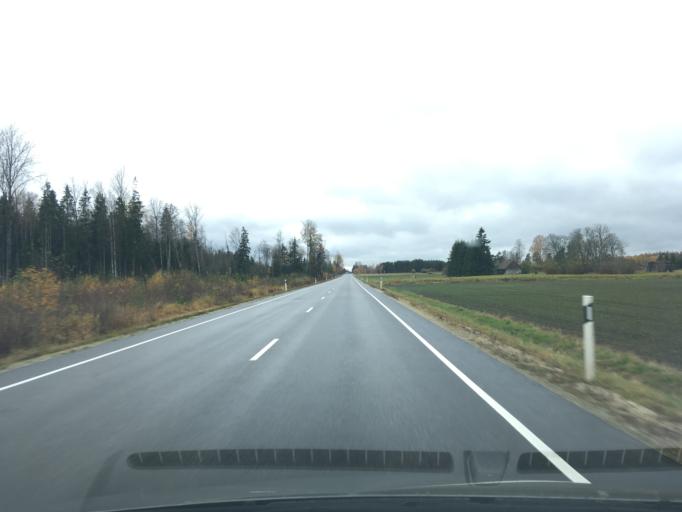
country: EE
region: Jogevamaa
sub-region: Tabivere vald
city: Tabivere
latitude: 58.4509
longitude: 26.5216
